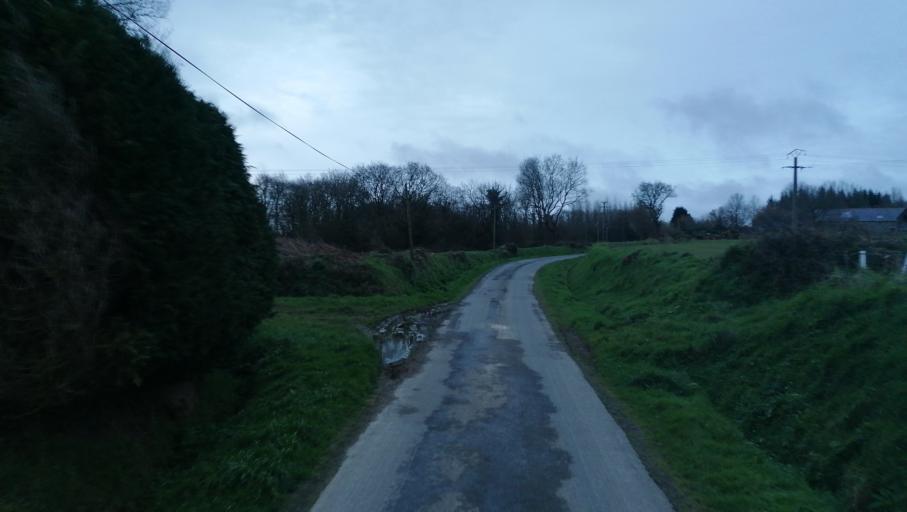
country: FR
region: Brittany
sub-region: Departement des Cotes-d'Armor
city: Goudelin
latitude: 48.5780
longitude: -3.0536
